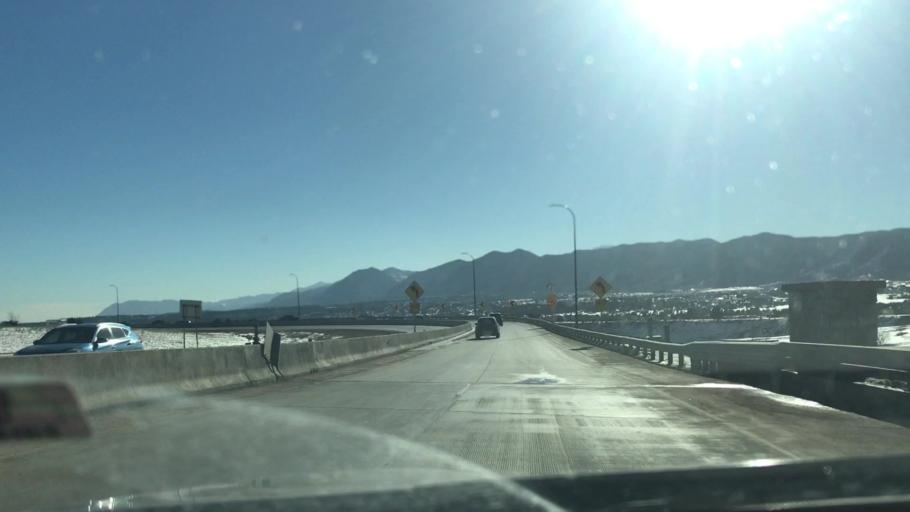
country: US
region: Colorado
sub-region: El Paso County
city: Monument
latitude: 39.0897
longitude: -104.8645
